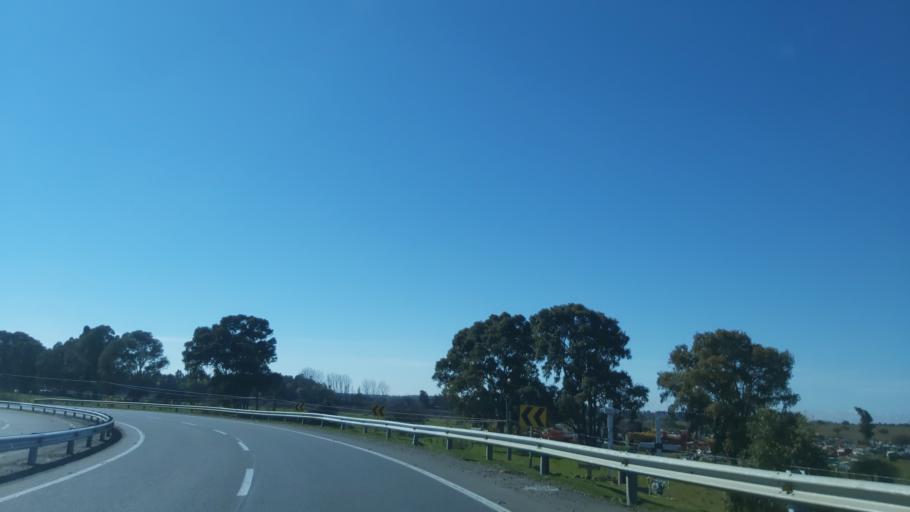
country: CL
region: Biobio
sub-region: Provincia de Nuble
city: Bulnes
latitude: -36.6562
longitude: -72.2281
